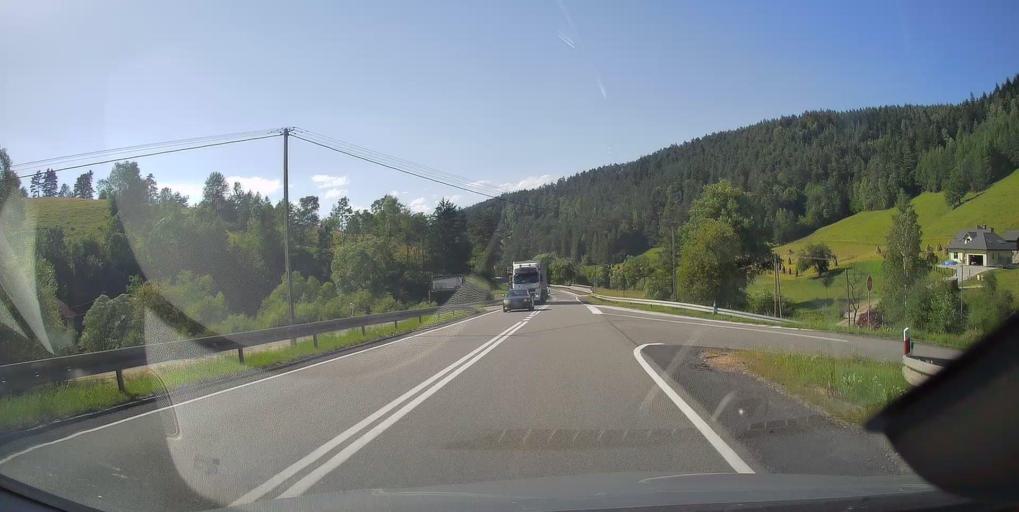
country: PL
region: Lesser Poland Voivodeship
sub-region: Powiat nowosadecki
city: Krynica-Zdroj
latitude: 49.4756
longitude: 20.9320
